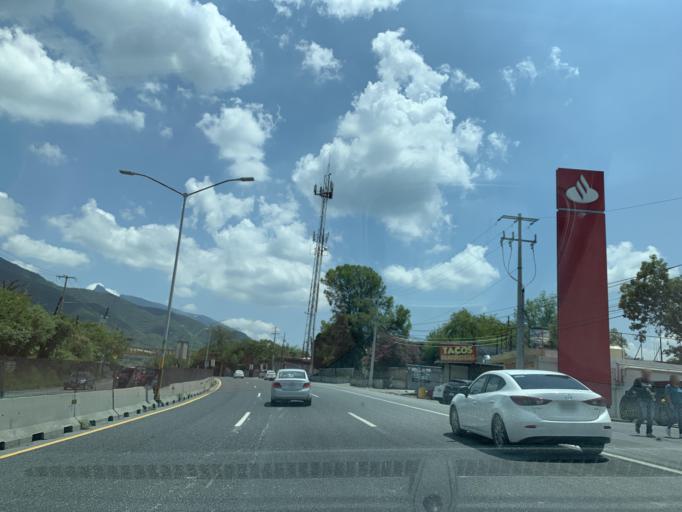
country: MX
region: Nuevo Leon
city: Santiago
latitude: 25.3991
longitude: -100.1305
